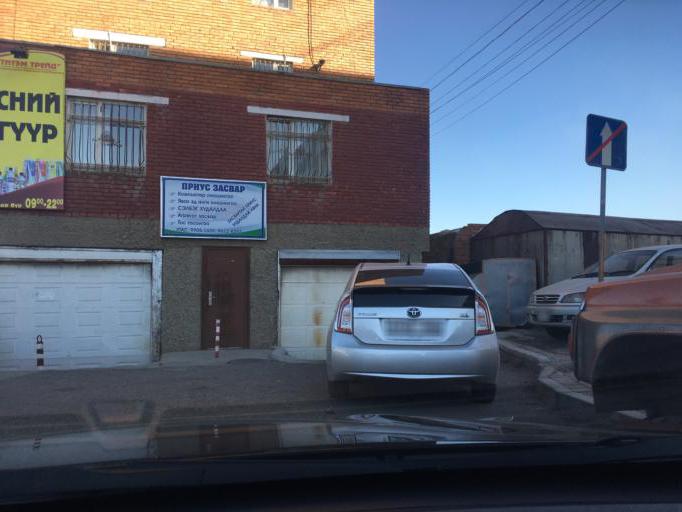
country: MN
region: Ulaanbaatar
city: Ulaanbaatar
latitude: 47.9247
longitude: 106.8710
